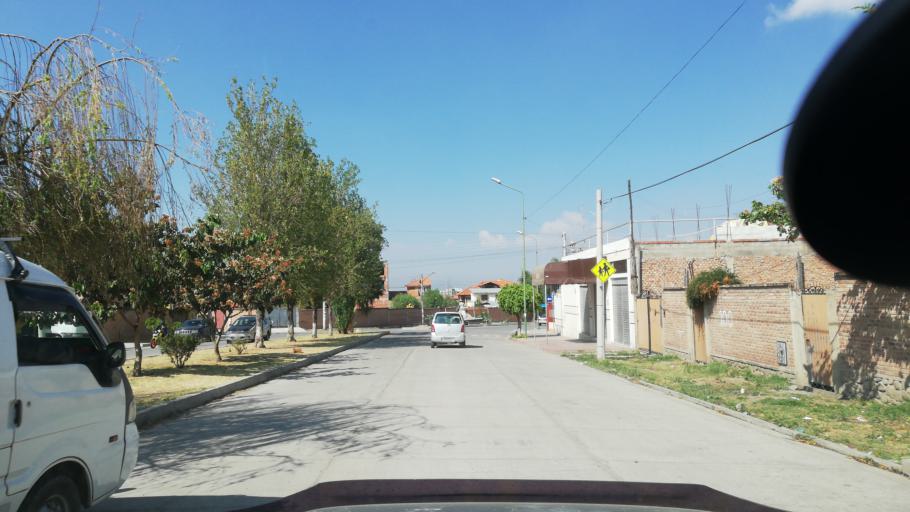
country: BO
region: Cochabamba
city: Cochabamba
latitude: -17.3597
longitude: -66.1866
